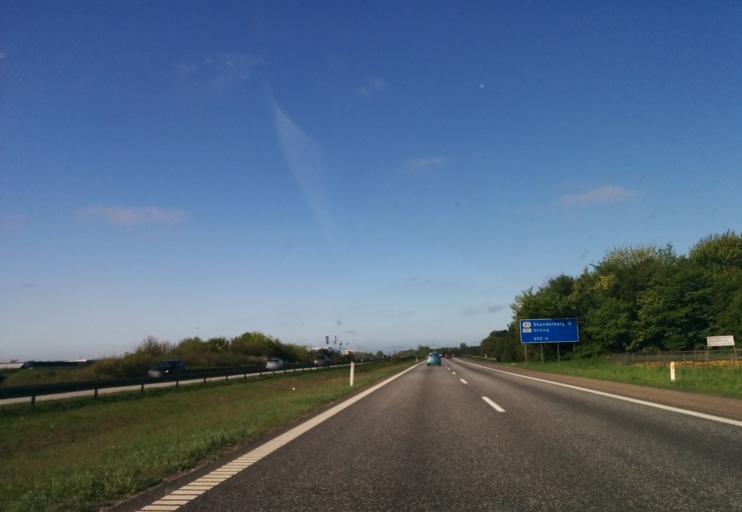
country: DK
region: Central Jutland
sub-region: Skanderborg Kommune
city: Stilling
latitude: 56.0731
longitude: 9.9937
